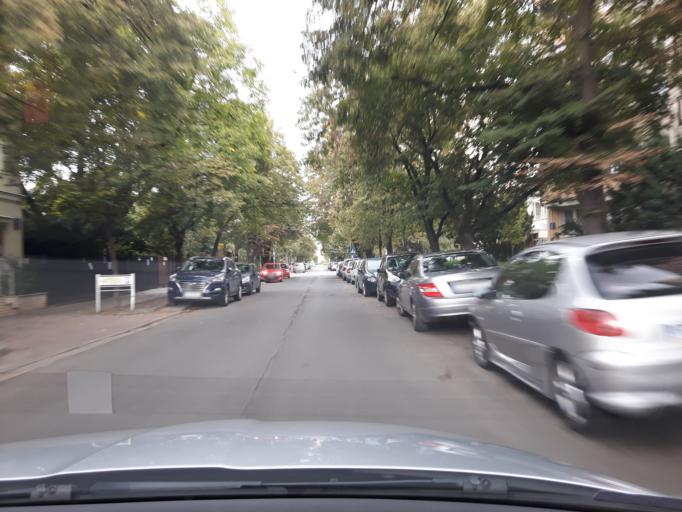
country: PL
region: Masovian Voivodeship
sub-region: Warszawa
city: Praga Poludnie
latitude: 52.2228
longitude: 21.0655
